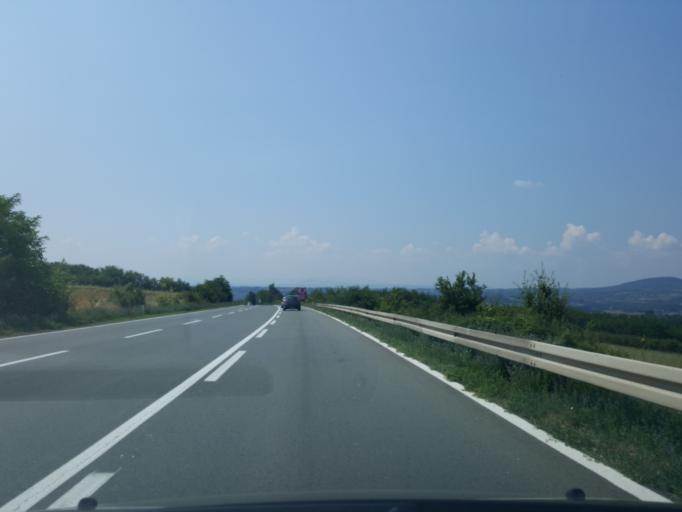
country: RS
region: Central Serbia
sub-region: Belgrade
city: Sopot
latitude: 44.5182
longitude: 20.6530
